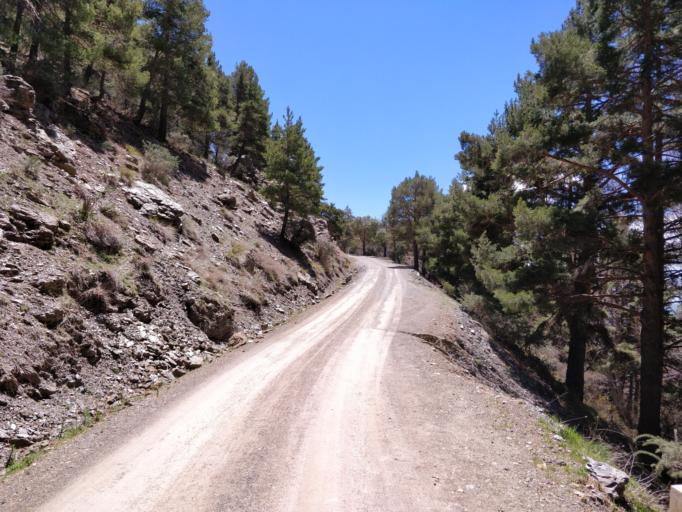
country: ES
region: Andalusia
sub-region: Provincia de Granada
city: Soportujar
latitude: 36.9685
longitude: -3.4090
